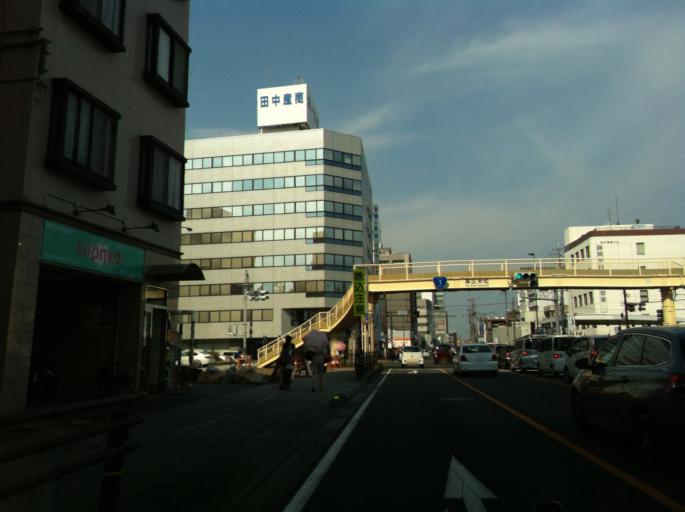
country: JP
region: Shizuoka
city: Shizuoka-shi
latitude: 34.9746
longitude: 138.3929
